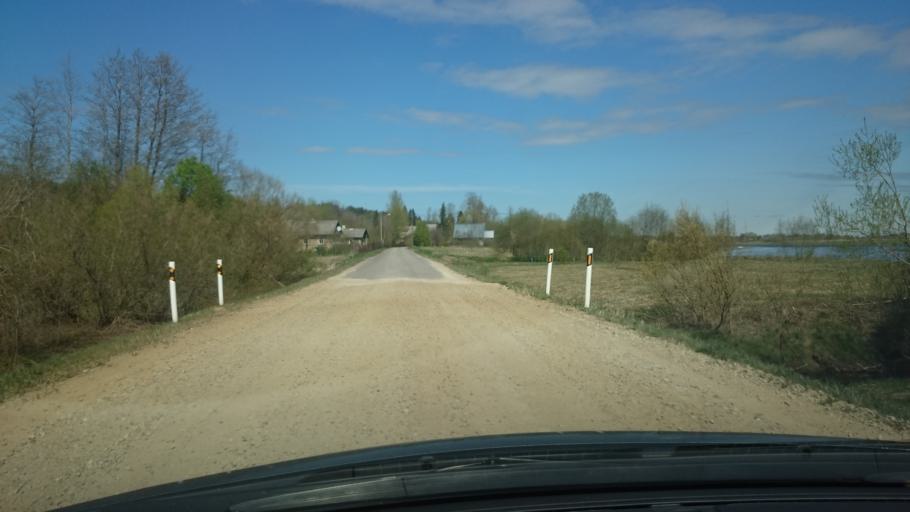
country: EE
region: Ida-Virumaa
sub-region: Sillamaee linn
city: Sillamae
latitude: 59.1160
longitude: 27.7986
